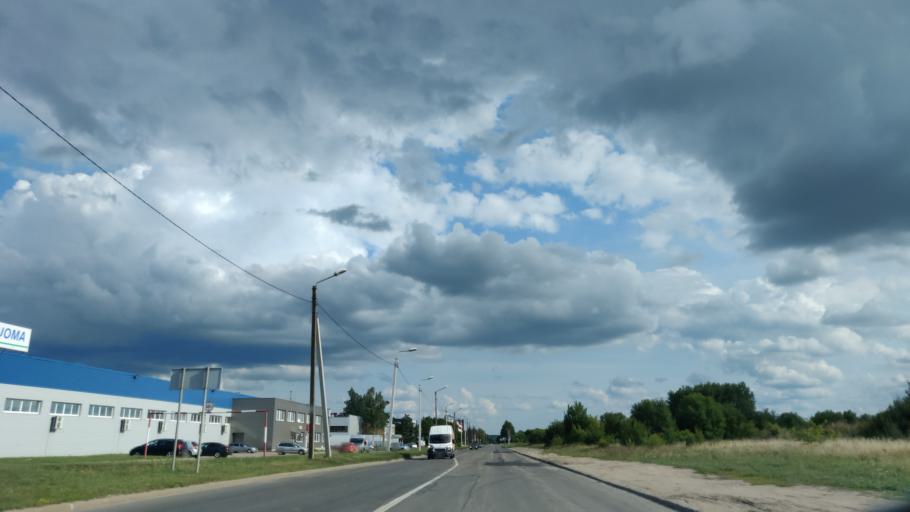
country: LT
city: Baltoji Voke
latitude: 54.6290
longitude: 25.1374
